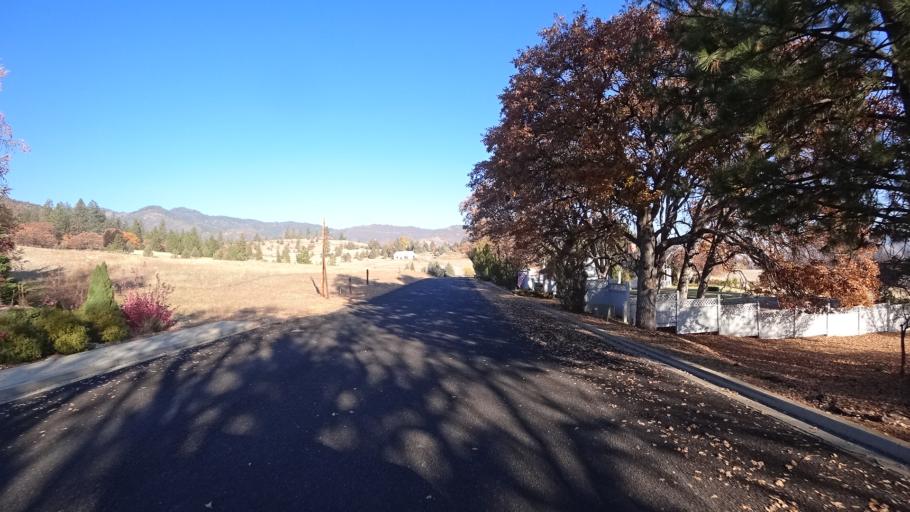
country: US
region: California
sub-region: Siskiyou County
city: Yreka
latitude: 41.7256
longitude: -122.6507
